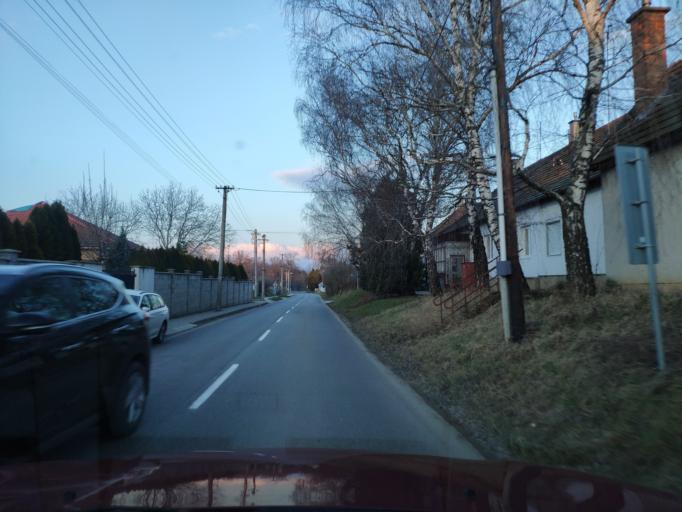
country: SK
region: Nitriansky
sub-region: Okres Nitra
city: Nitra
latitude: 48.2372
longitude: 18.1173
